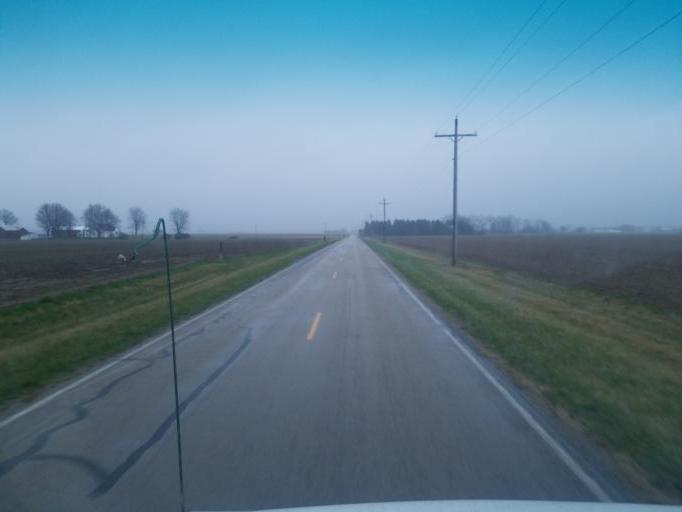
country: US
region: Ohio
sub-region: Henry County
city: Napoleon
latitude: 41.4132
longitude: -84.2345
